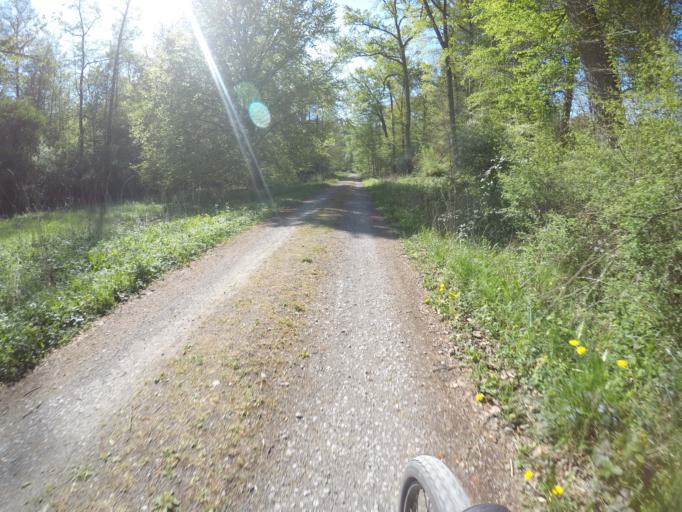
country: DE
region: Baden-Wuerttemberg
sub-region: Tuebingen Region
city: Dettenhausen
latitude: 48.5704
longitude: 9.0948
